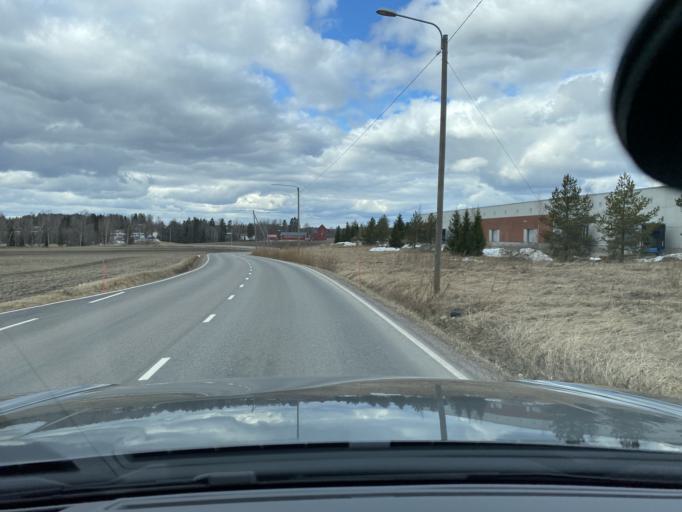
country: FI
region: Uusimaa
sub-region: Helsinki
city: Kilo
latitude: 60.3350
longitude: 24.8336
